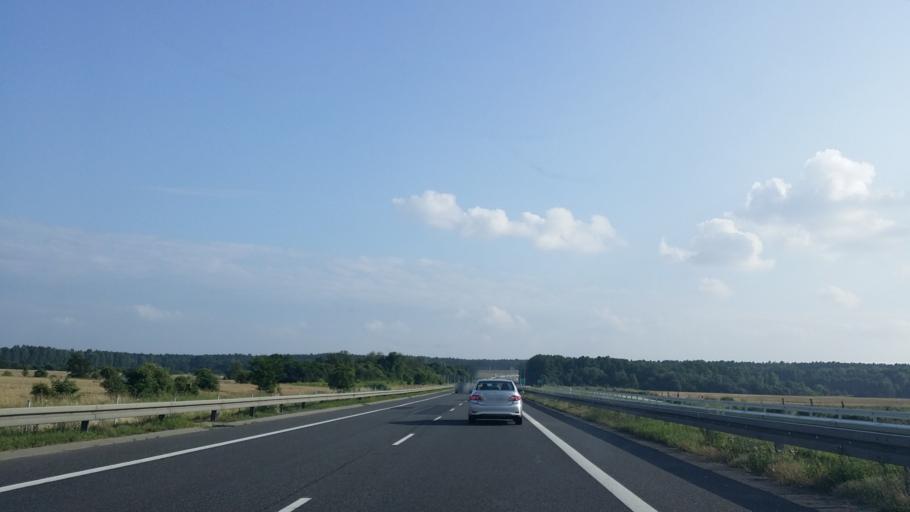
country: PL
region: Lubusz
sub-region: Powiat miedzyrzecki
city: Miedzyrzecz
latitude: 52.4312
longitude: 15.5553
